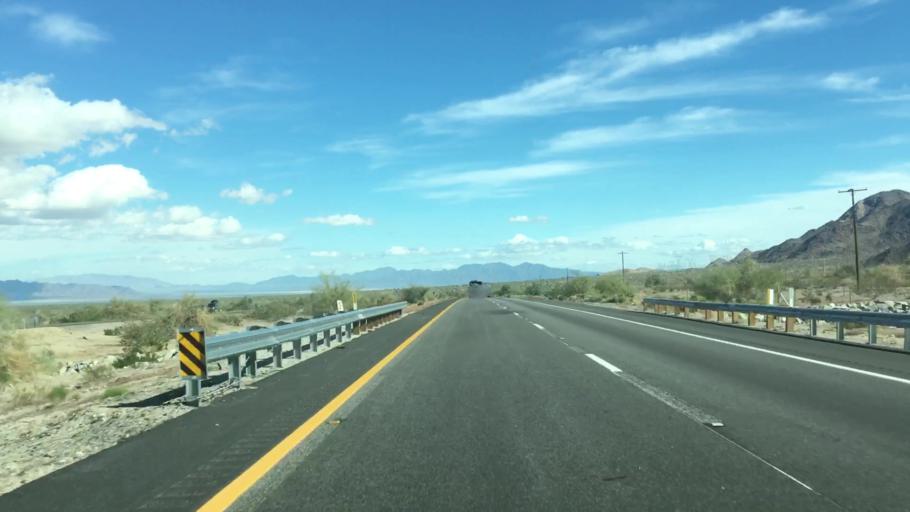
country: US
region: California
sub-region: Imperial County
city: Niland
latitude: 33.6883
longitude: -115.5154
